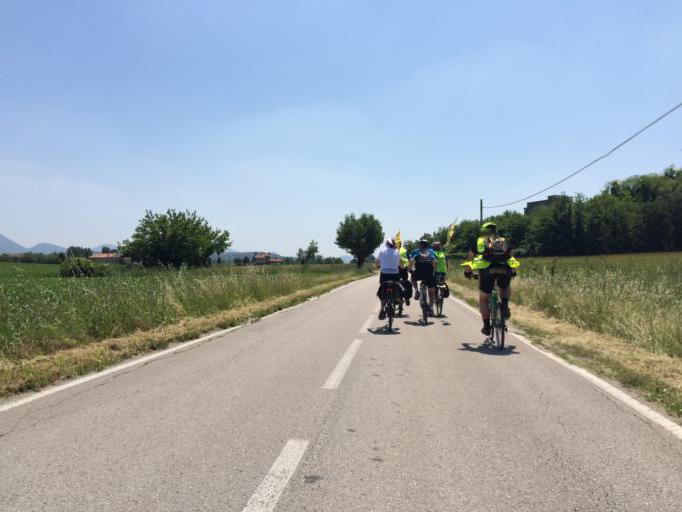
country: IT
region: Veneto
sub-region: Provincia di Vicenza
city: Villaga
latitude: 45.3937
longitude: 11.5457
